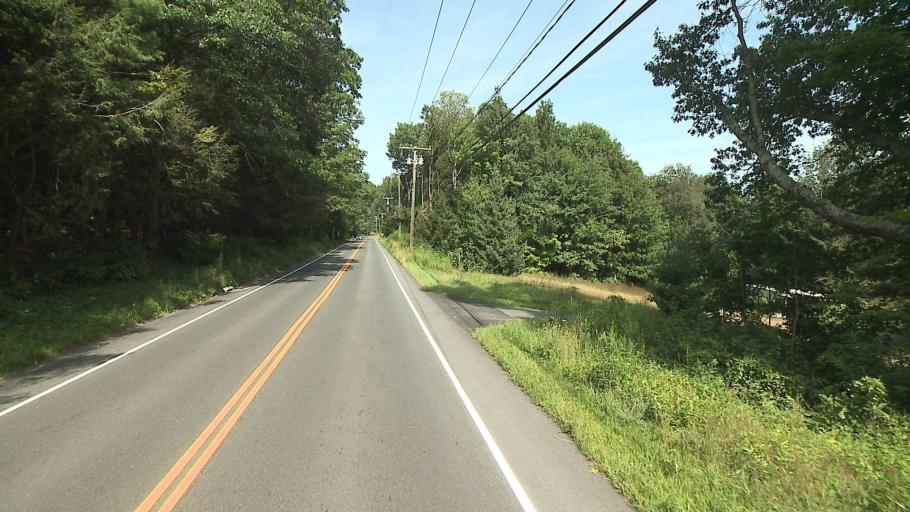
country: US
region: Connecticut
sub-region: Litchfield County
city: Bethlehem Village
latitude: 41.6061
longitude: -73.1764
